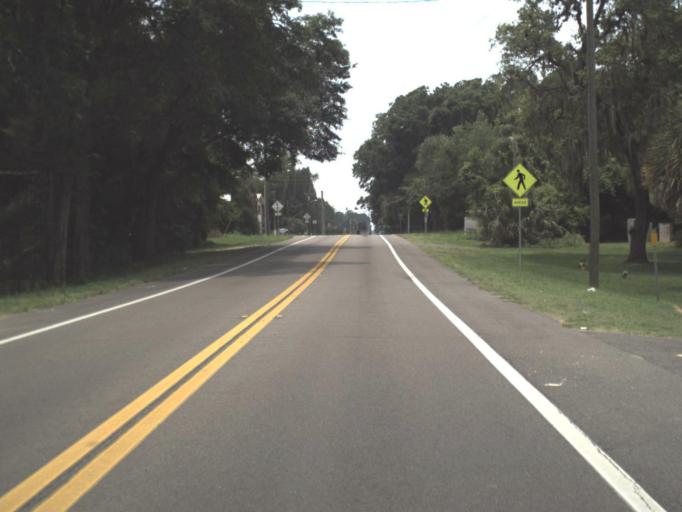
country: US
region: Florida
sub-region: Levy County
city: Chiefland
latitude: 29.4966
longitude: -82.8706
